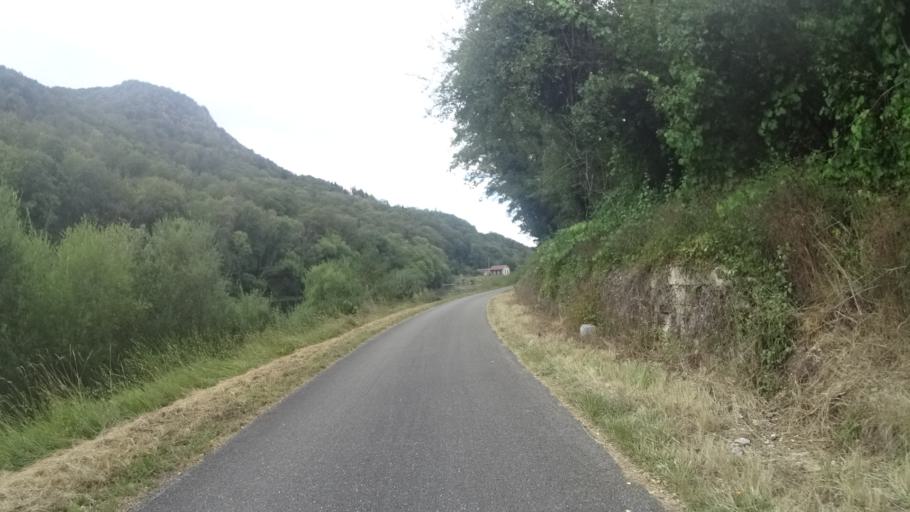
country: FR
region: Franche-Comte
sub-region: Departement du Doubs
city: Baume-les-Dames
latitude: 47.3301
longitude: 6.3096
